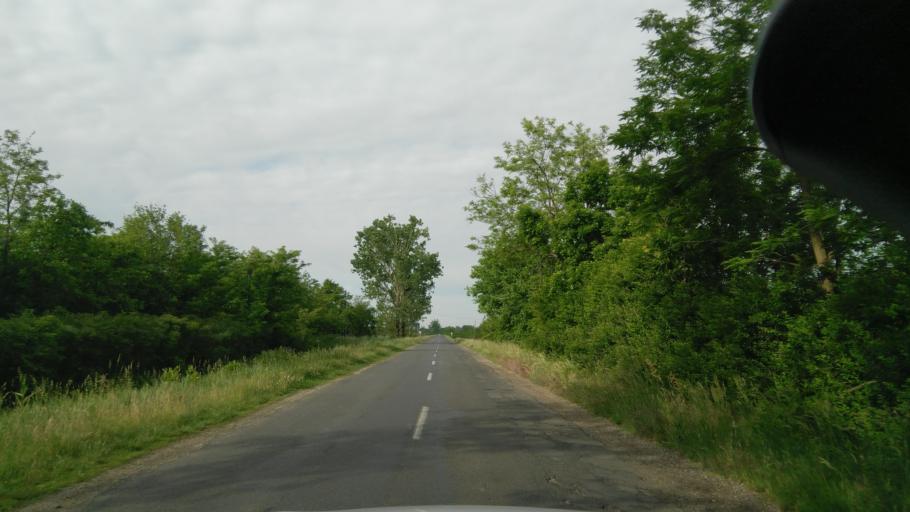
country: HU
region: Bekes
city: Gyula
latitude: 46.6021
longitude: 21.2388
